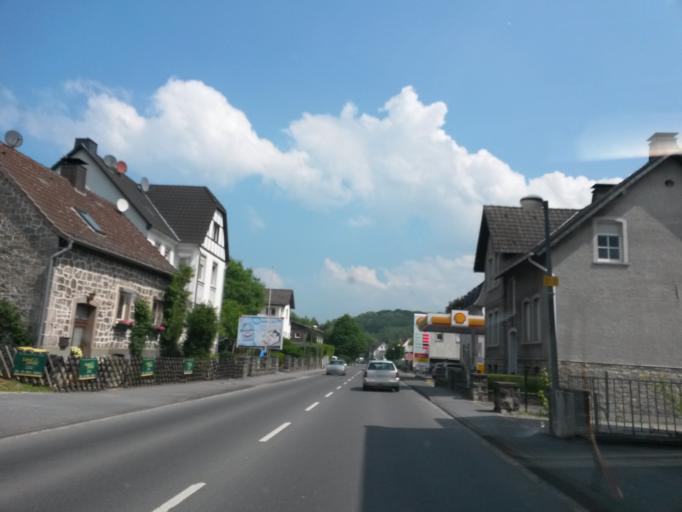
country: DE
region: North Rhine-Westphalia
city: Balve
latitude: 51.3328
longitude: 7.8654
